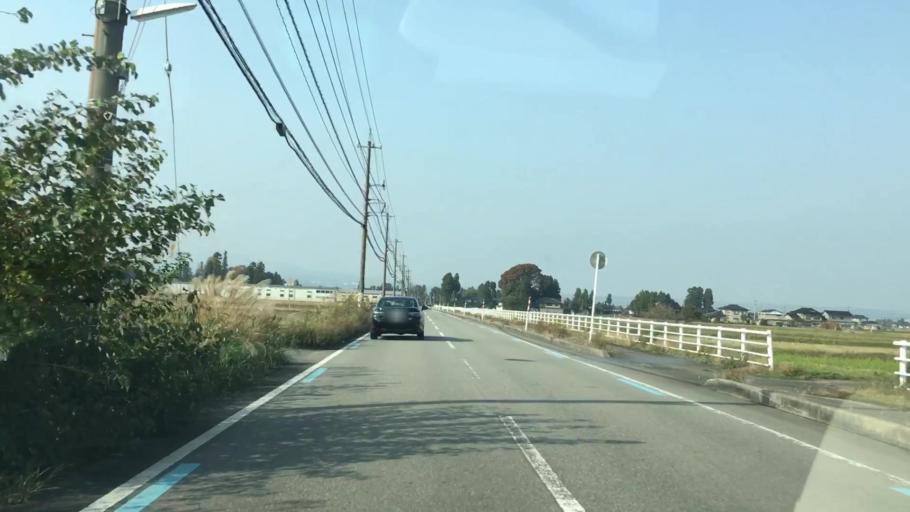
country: JP
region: Toyama
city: Toyama-shi
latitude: 36.6079
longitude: 137.2741
